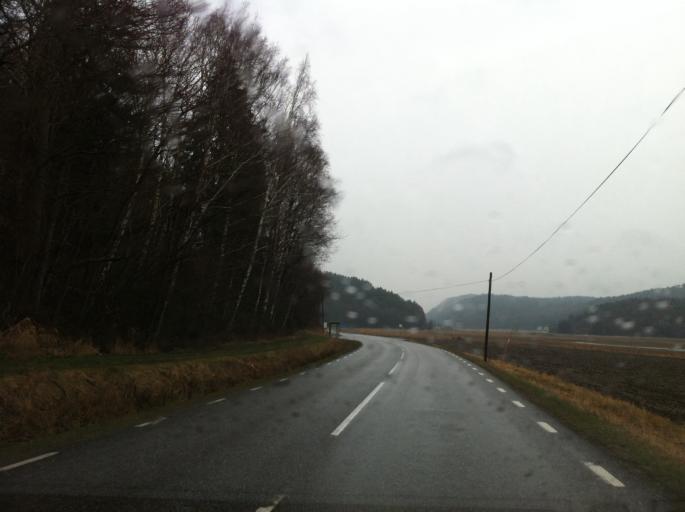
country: SE
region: Vaestra Goetaland
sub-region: Lysekils Kommun
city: Brastad
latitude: 58.4559
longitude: 11.4498
